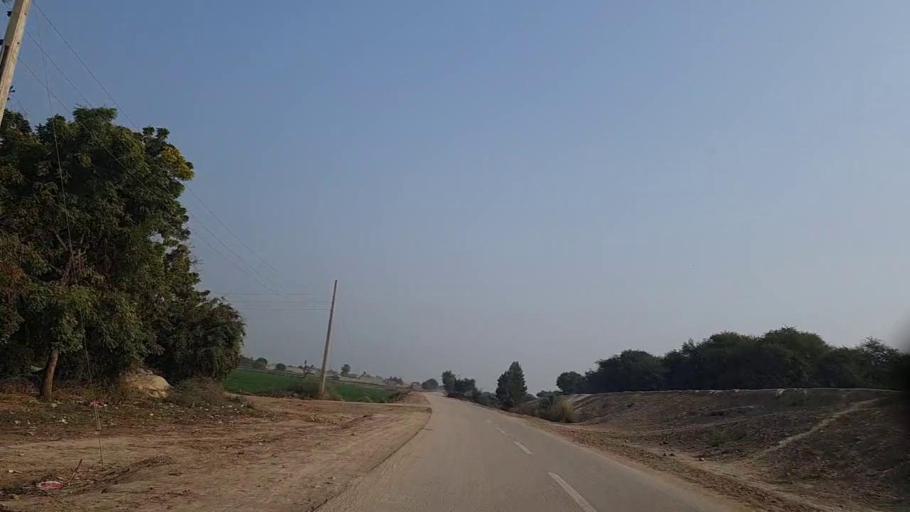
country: PK
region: Sindh
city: Sann
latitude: 26.1530
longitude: 68.1211
